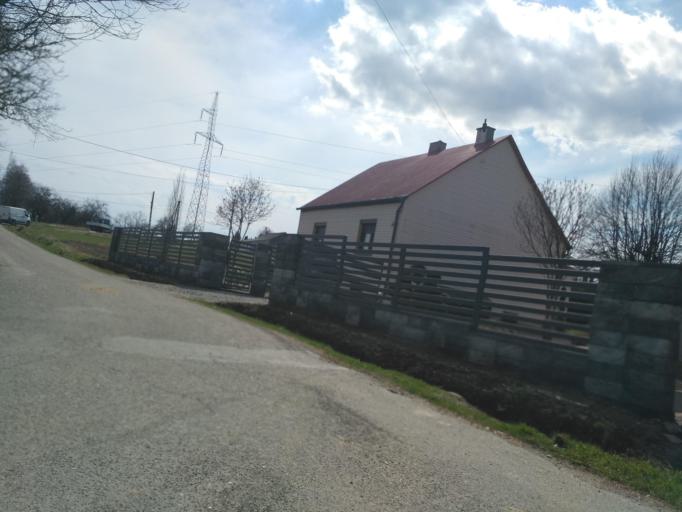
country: PL
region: Subcarpathian Voivodeship
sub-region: Powiat ropczycko-sedziszowski
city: Iwierzyce
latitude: 50.0494
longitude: 21.7311
